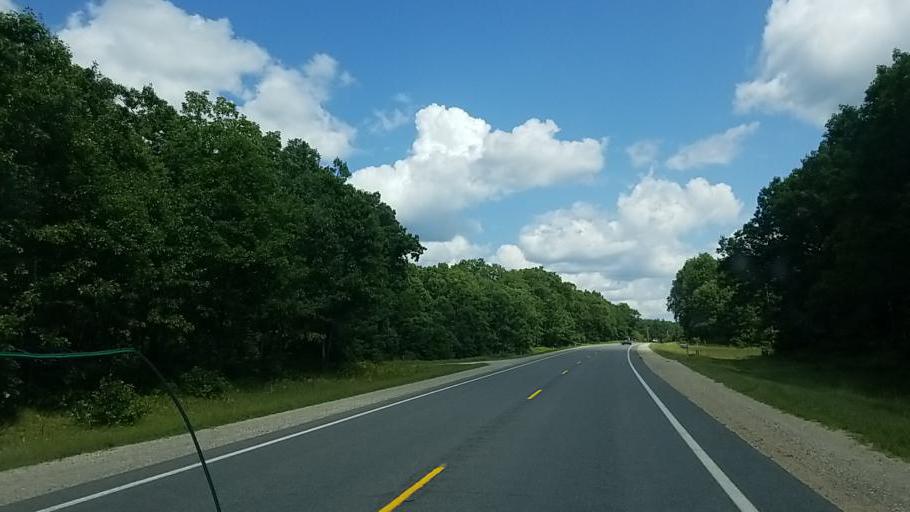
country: US
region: Michigan
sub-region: Newaygo County
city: Newaygo
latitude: 43.4062
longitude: -85.6820
